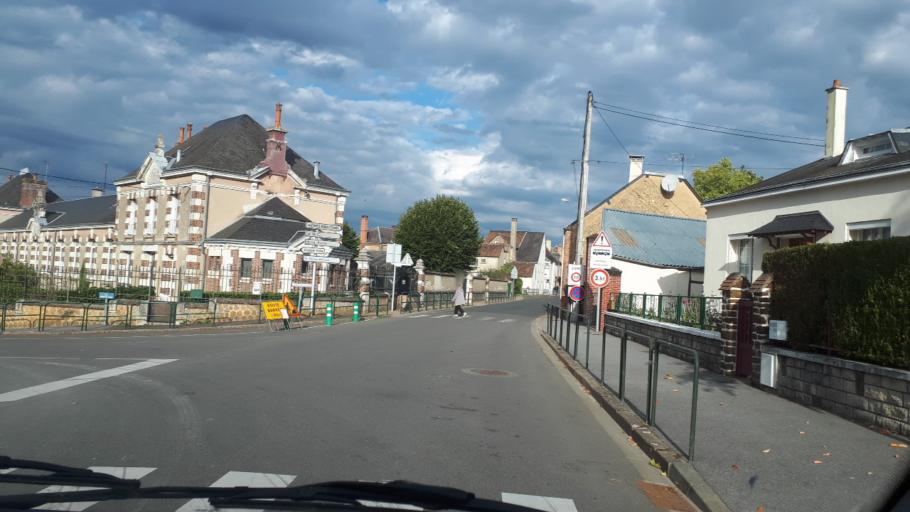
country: FR
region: Centre
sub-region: Departement du Loir-et-Cher
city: Mondoubleau
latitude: 47.9797
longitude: 0.8986
